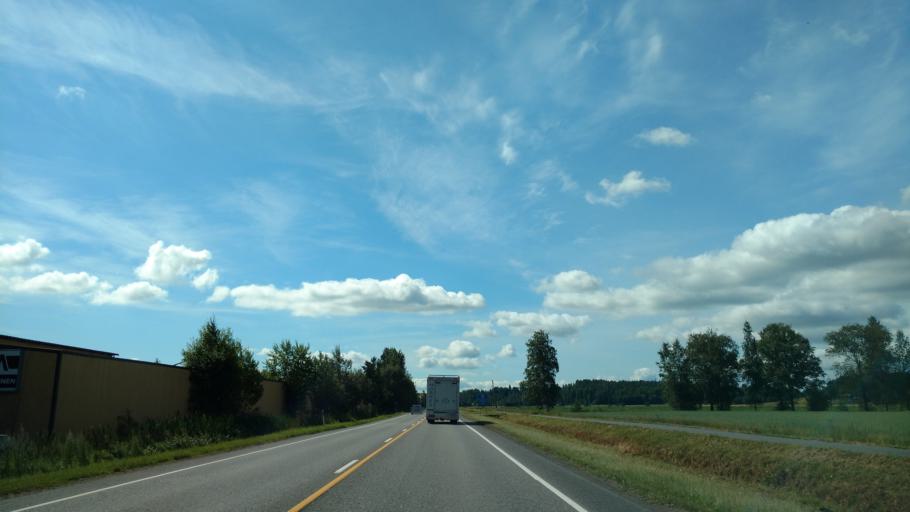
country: FI
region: Varsinais-Suomi
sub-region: Salo
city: Pernioe
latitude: 60.2325
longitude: 23.1240
